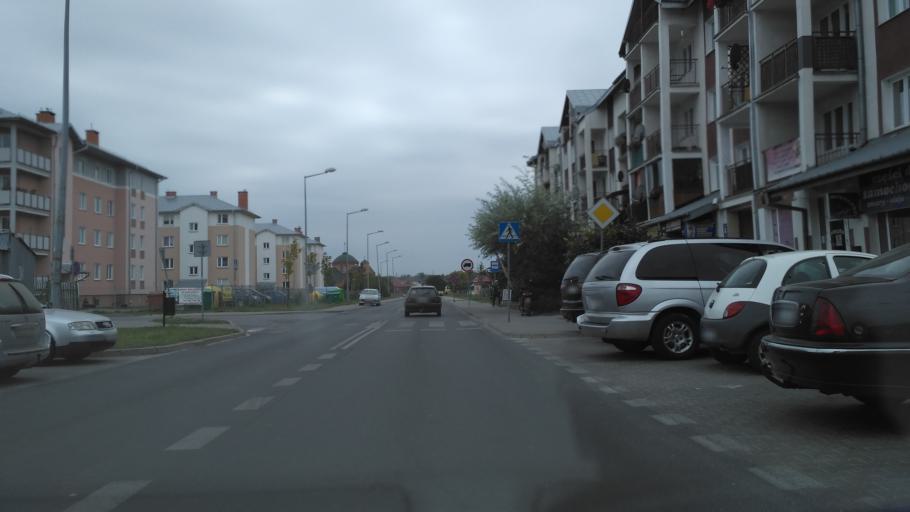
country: PL
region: Lublin Voivodeship
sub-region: Chelm
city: Chelm
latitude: 51.1300
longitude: 23.4660
